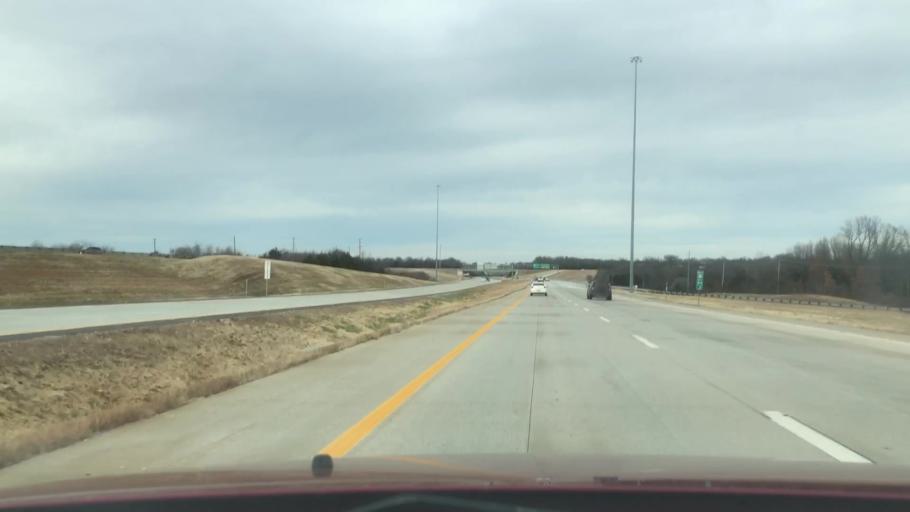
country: US
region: Missouri
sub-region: Greene County
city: Springfield
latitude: 37.2514
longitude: -93.2244
